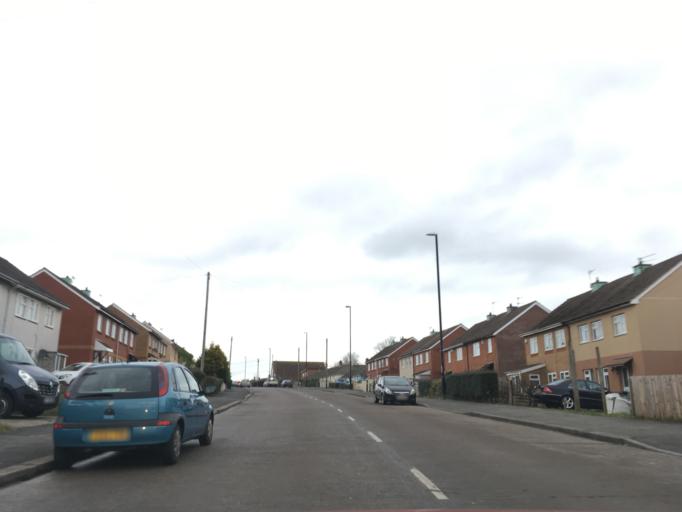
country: GB
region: England
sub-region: South Gloucestershire
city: Stoke Gifford
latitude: 51.4885
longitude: -2.5623
